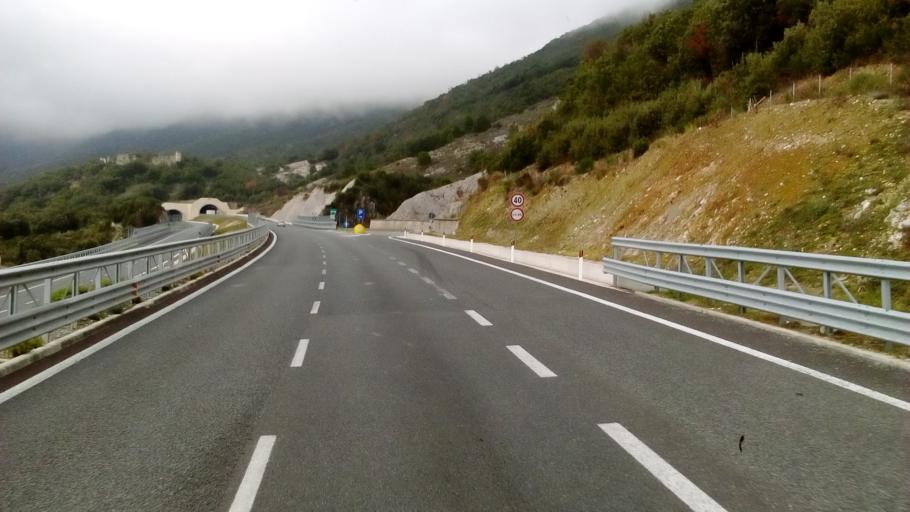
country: IT
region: Calabria
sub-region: Provincia di Cosenza
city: Morano Calabro
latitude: 39.8851
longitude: 16.1586
